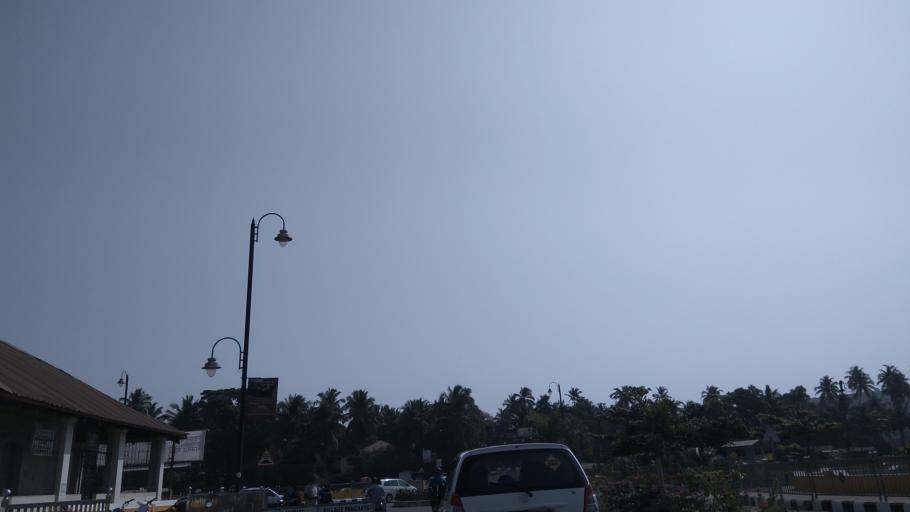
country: IN
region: Goa
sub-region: North Goa
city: Saligao
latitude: 15.5461
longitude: 73.7887
